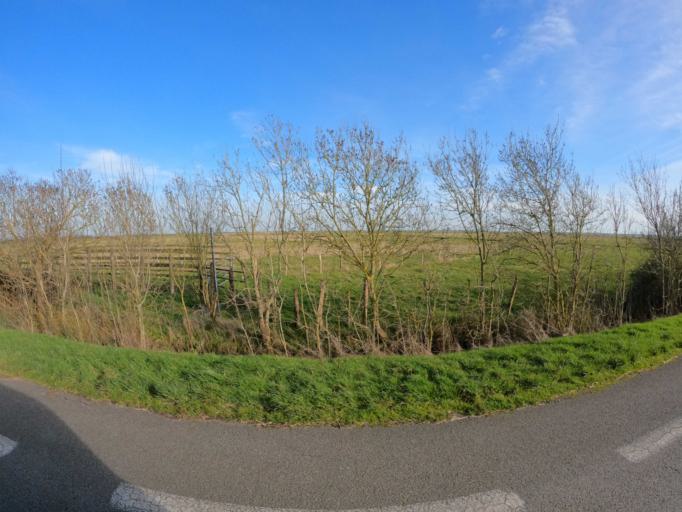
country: FR
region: Pays de la Loire
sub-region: Departement de la Vendee
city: Angles
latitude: 46.3824
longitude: -1.4071
